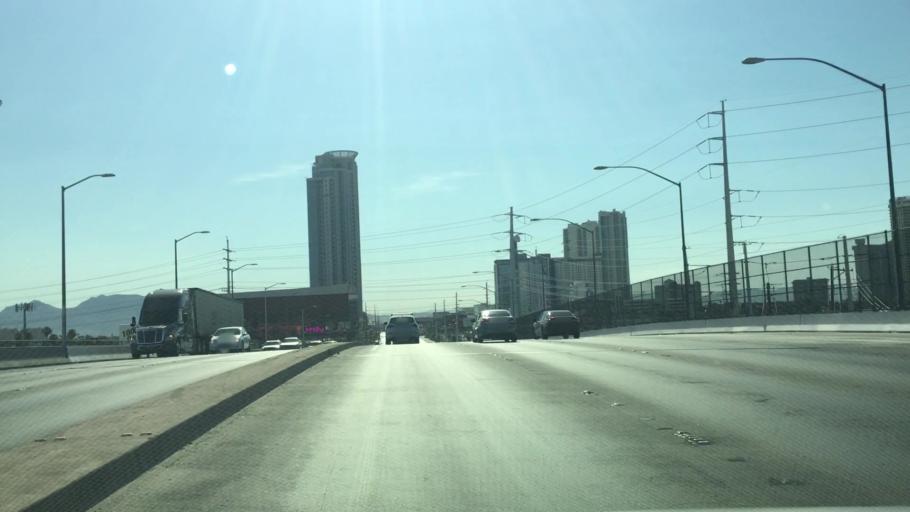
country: US
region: Nevada
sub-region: Clark County
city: Las Vegas
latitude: 36.1440
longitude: -115.1665
